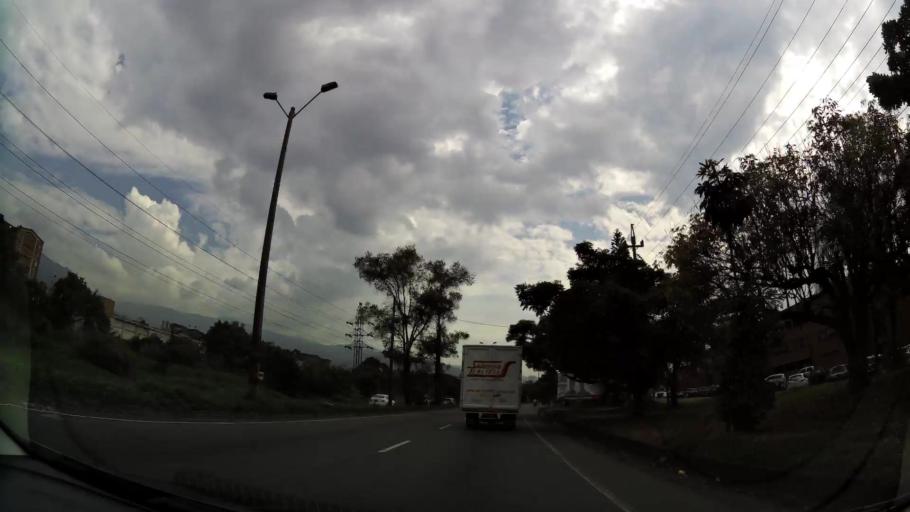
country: CO
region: Antioquia
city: Envigado
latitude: 6.1894
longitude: -75.5836
